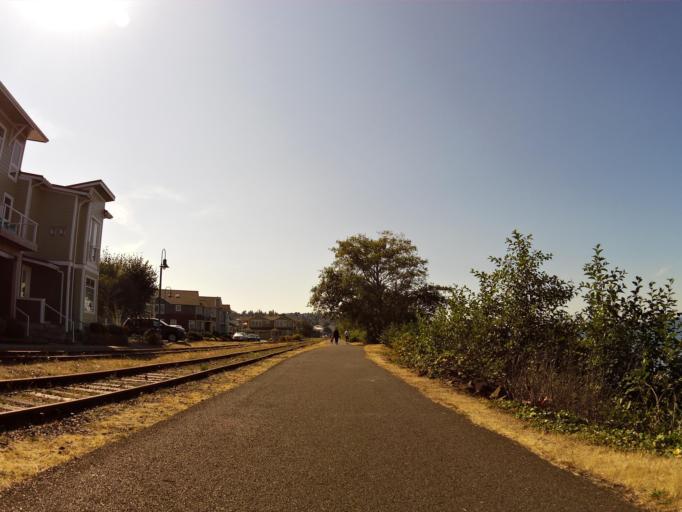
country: US
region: Oregon
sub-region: Clatsop County
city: Astoria
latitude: 46.1918
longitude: -123.8130
